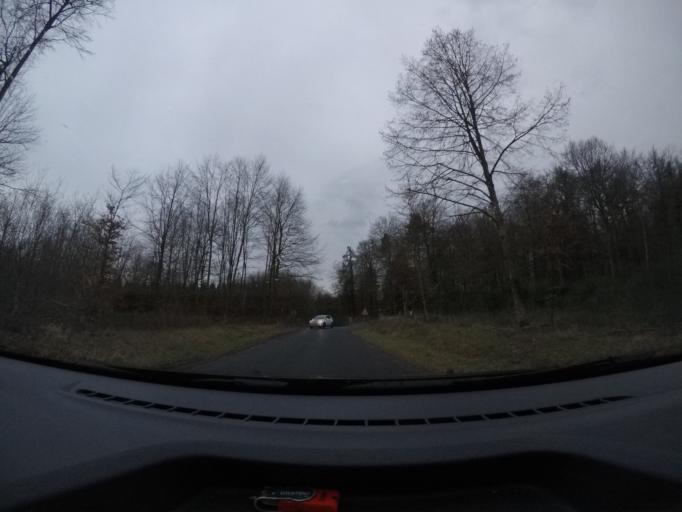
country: BE
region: Wallonia
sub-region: Province du Luxembourg
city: Tintigny
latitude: 49.6805
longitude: 5.4981
